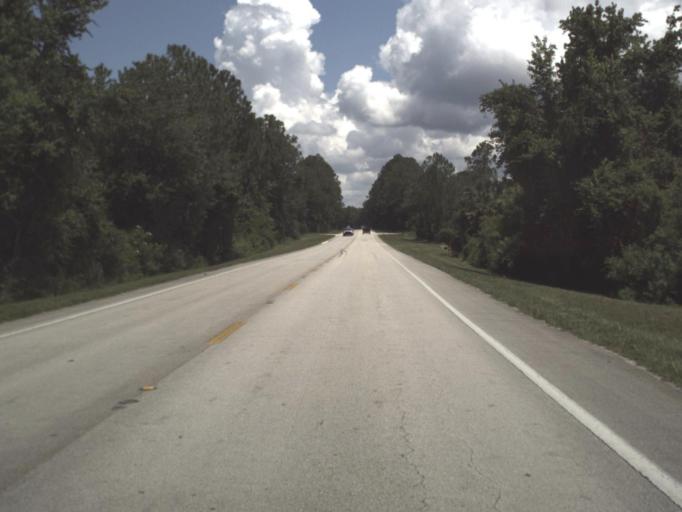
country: US
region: Florida
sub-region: Putnam County
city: Crescent City
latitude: 29.3817
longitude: -81.5088
